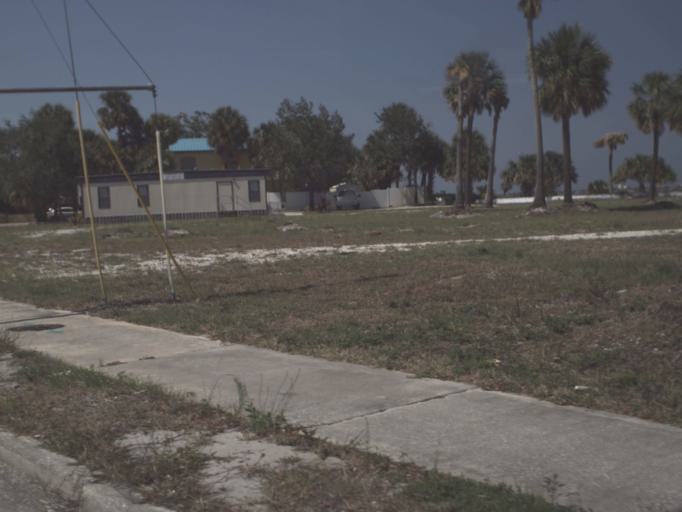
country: US
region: Florida
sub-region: Brevard County
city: Melbourne
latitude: 28.0864
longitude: -80.6068
